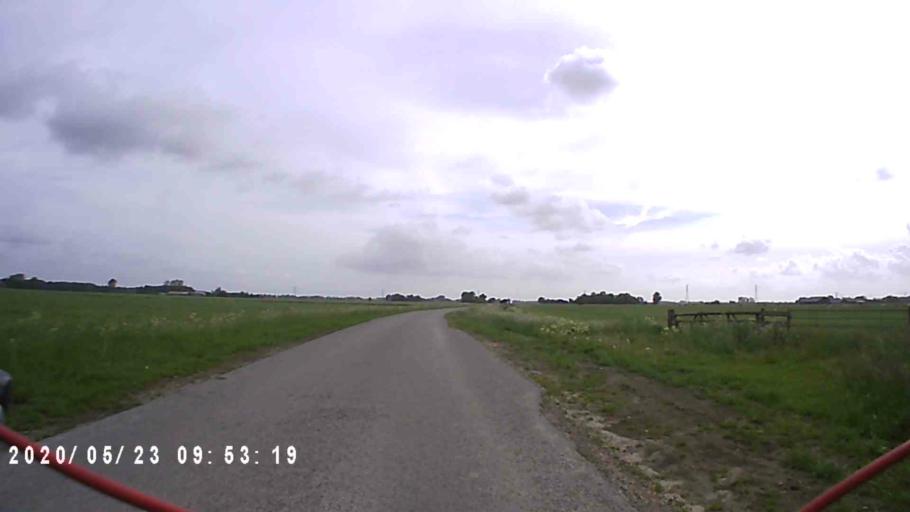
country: NL
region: Groningen
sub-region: Gemeente Appingedam
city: Appingedam
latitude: 53.2988
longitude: 6.7901
